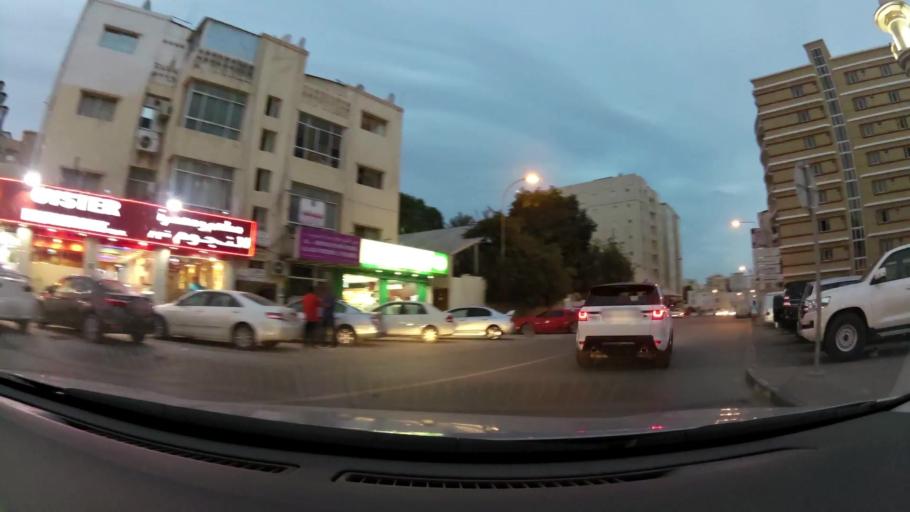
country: QA
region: Baladiyat ad Dawhah
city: Doha
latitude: 25.2702
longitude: 51.5207
